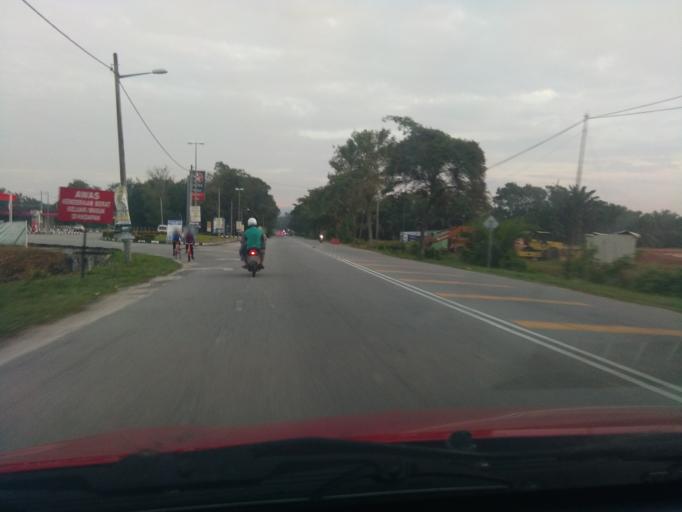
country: MY
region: Kedah
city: Kulim
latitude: 5.2238
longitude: 100.6883
